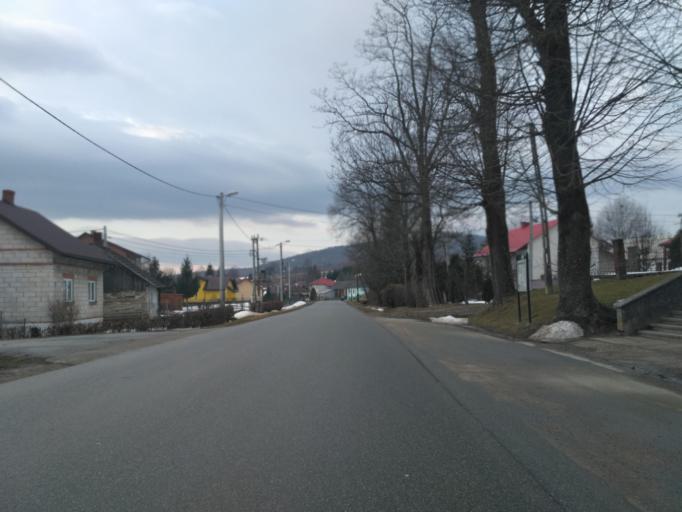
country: PL
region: Subcarpathian Voivodeship
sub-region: Powiat brzozowski
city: Dydnia
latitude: 49.6307
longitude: 22.1640
